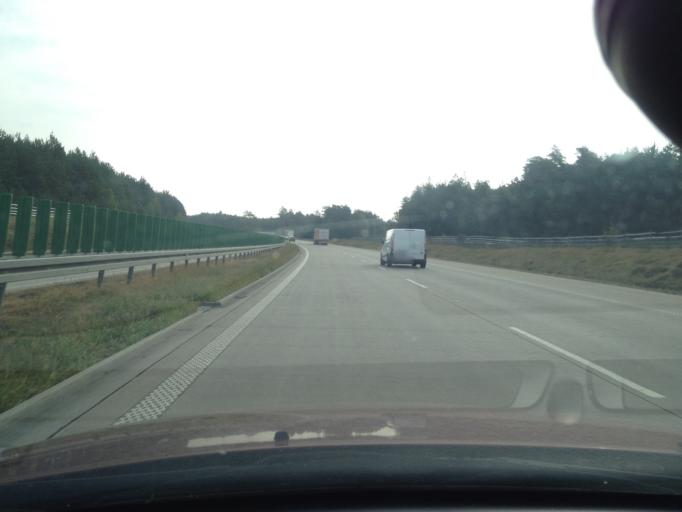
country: PL
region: Lower Silesian Voivodeship
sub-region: Powiat boleslawiecki
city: Nowogrodziec
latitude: 51.2681
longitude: 15.4241
